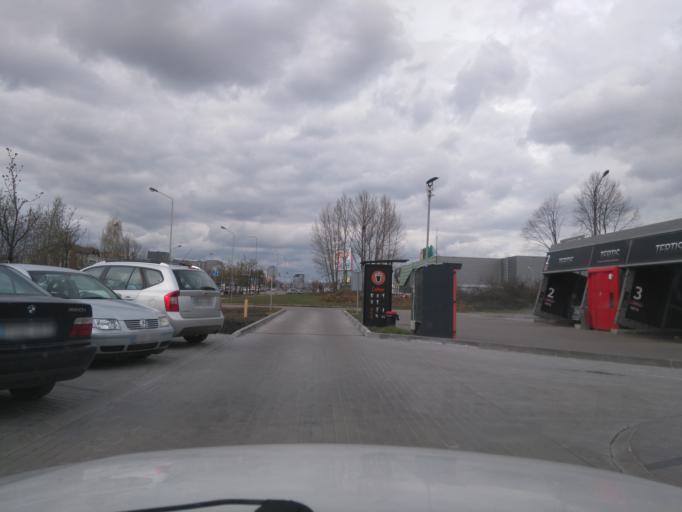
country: LT
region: Kauno apskritis
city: Dainava (Kaunas)
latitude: 54.9069
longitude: 23.9813
